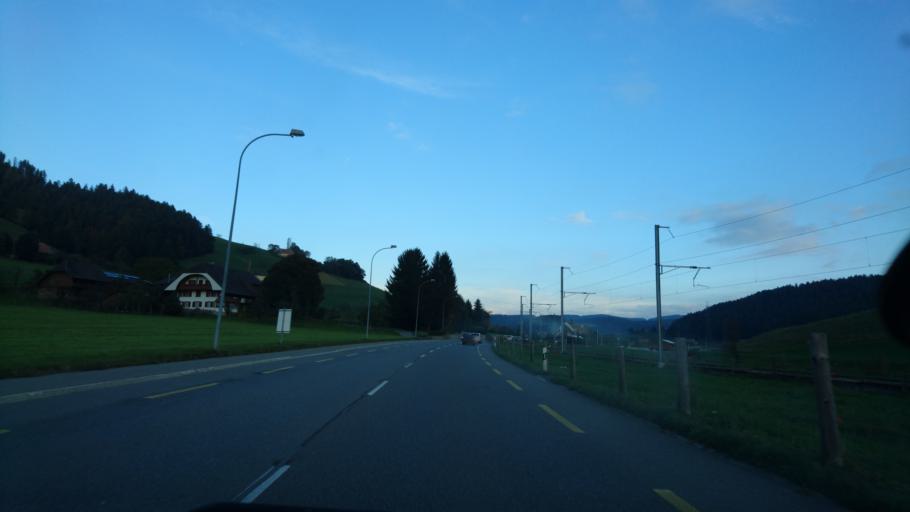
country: CH
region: Bern
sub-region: Bern-Mittelland District
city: Zaziwil
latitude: 46.9025
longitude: 7.6669
